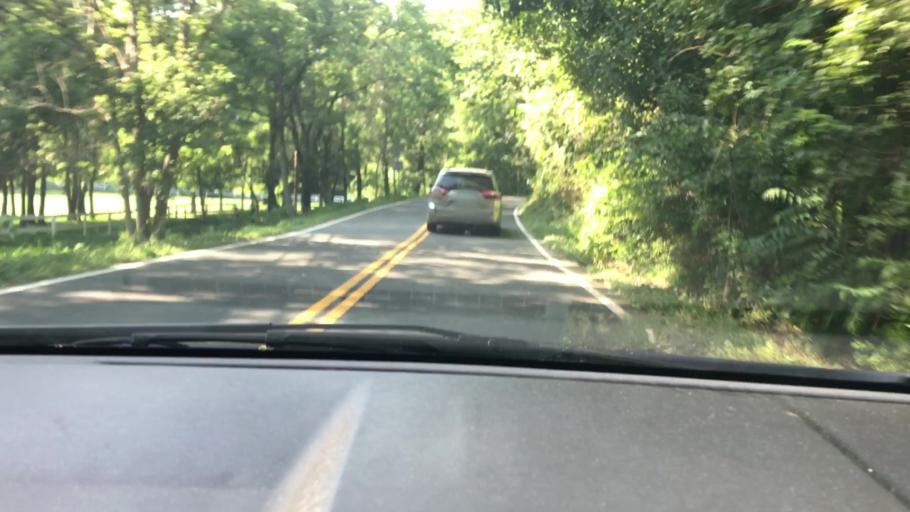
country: US
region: Virginia
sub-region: Fairfax County
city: Great Falls
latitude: 38.9978
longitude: -77.2629
